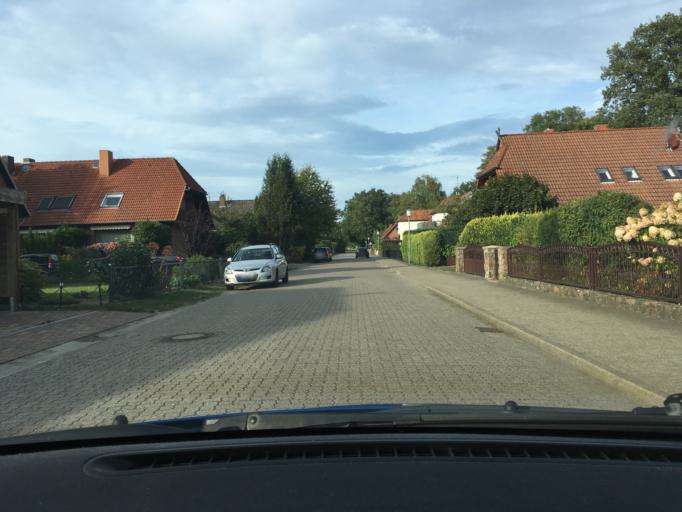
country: DE
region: Lower Saxony
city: Fassberg
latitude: 52.8807
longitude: 10.1189
